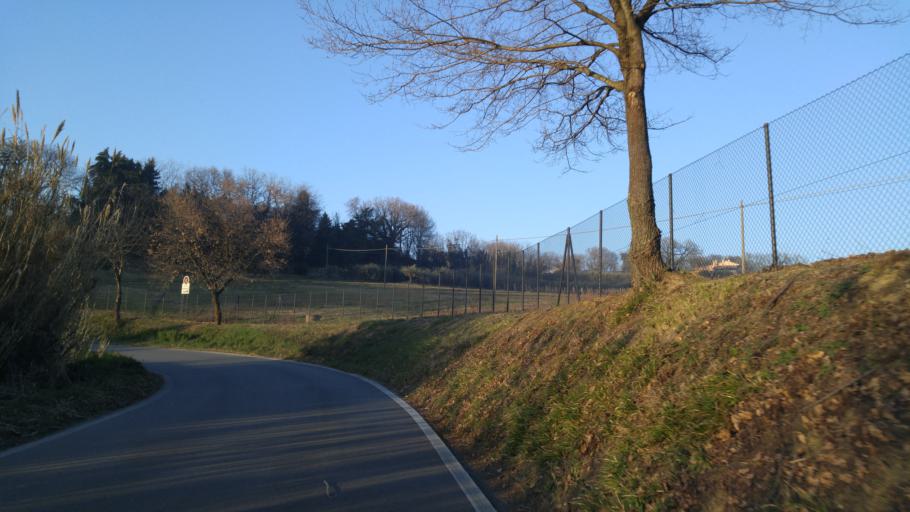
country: IT
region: The Marches
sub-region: Provincia di Pesaro e Urbino
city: Fenile
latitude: 43.8577
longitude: 12.9651
